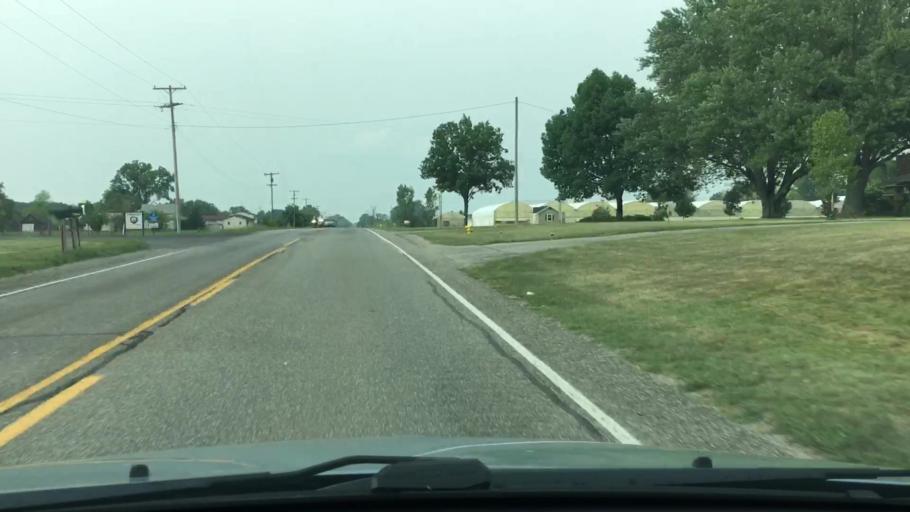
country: US
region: Michigan
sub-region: Ottawa County
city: Hudsonville
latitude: 42.8660
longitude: -85.9009
